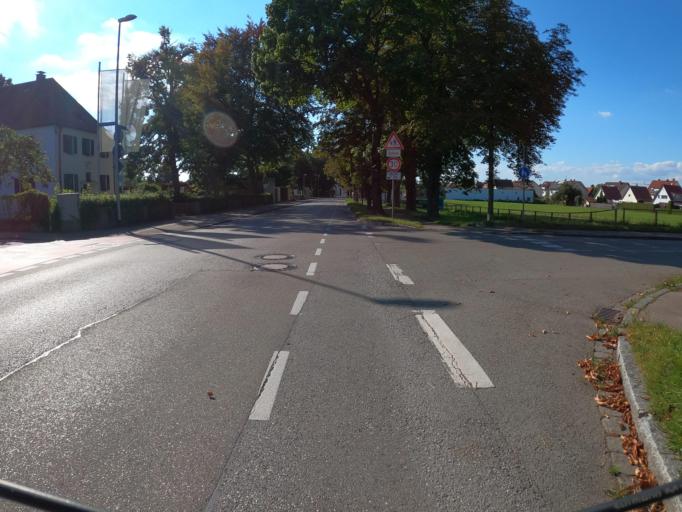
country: DE
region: Bavaria
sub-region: Swabia
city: Weissenhorn
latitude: 48.3042
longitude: 10.1672
